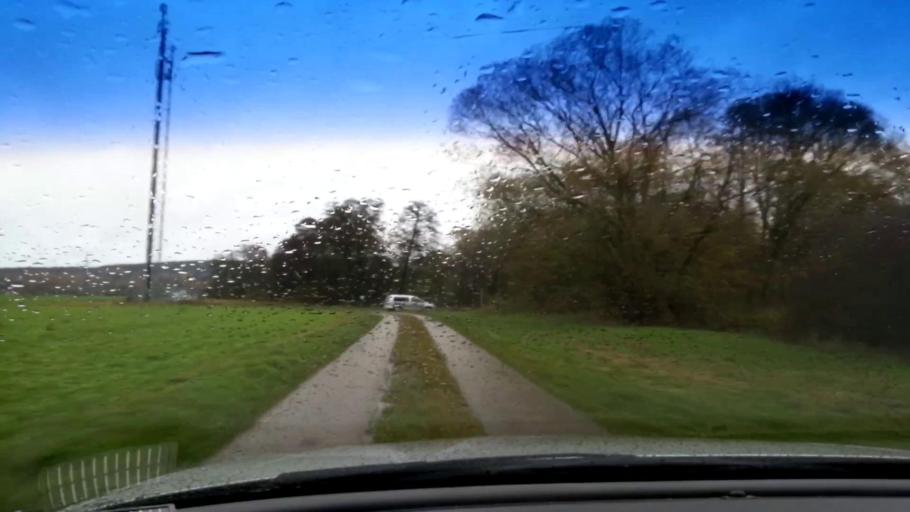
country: DE
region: Bavaria
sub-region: Upper Franconia
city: Bischberg
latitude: 49.9206
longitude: 10.8375
